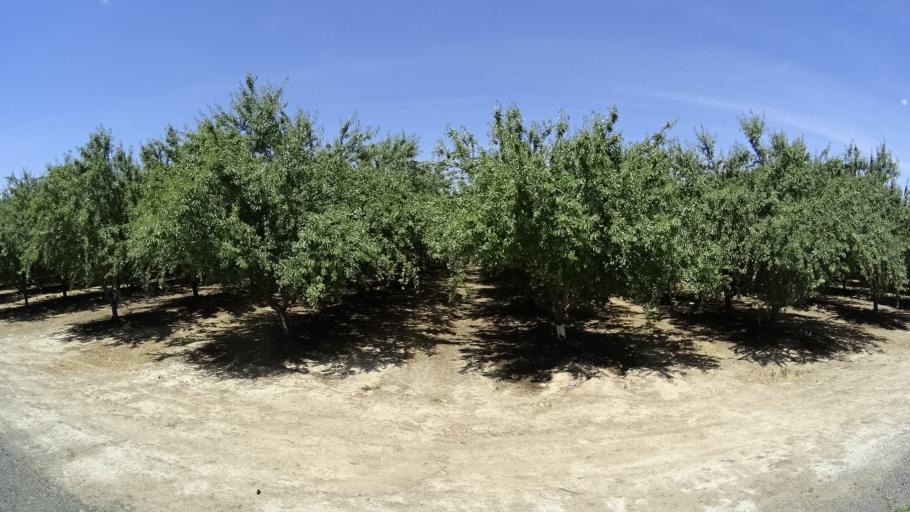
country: US
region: California
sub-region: Kings County
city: Lemoore
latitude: 36.2837
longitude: -119.7573
